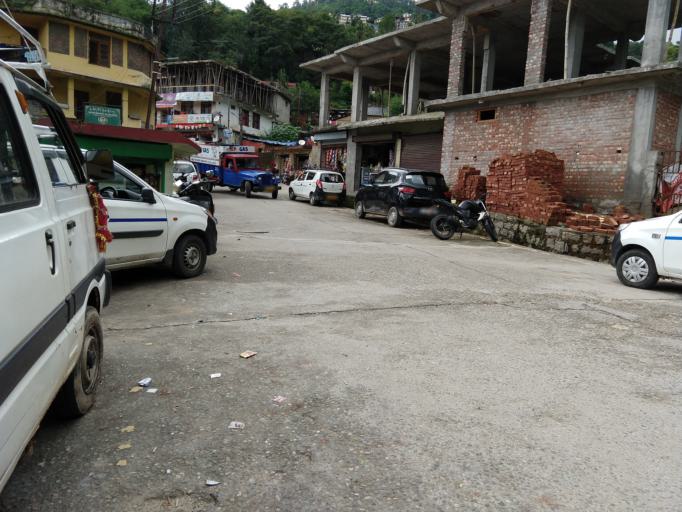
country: IN
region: Himachal Pradesh
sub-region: Kangra
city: Dharmsala
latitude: 32.2213
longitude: 76.3291
